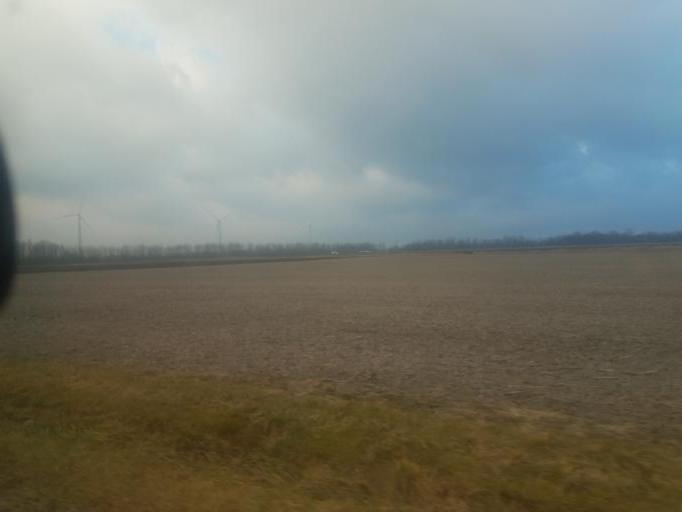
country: US
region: Ohio
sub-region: Marion County
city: Marion
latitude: 40.5981
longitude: -83.1688
